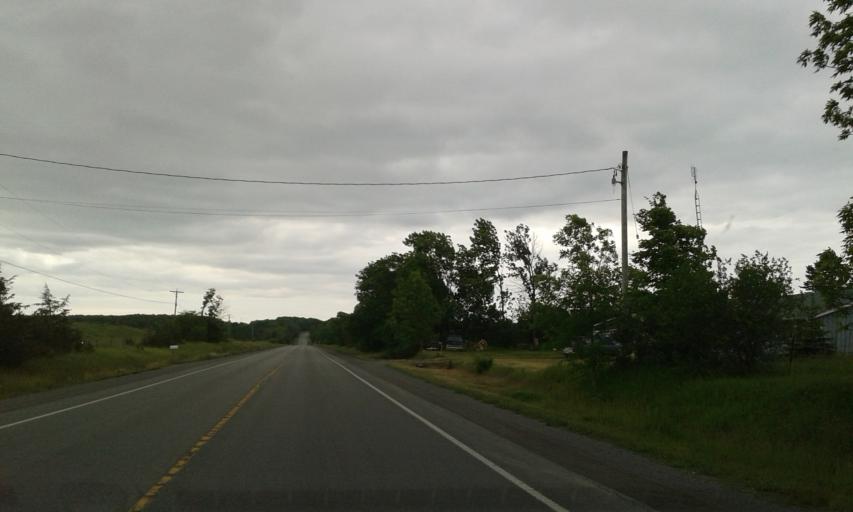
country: CA
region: Ontario
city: Quinte West
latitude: 43.9838
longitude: -77.5139
